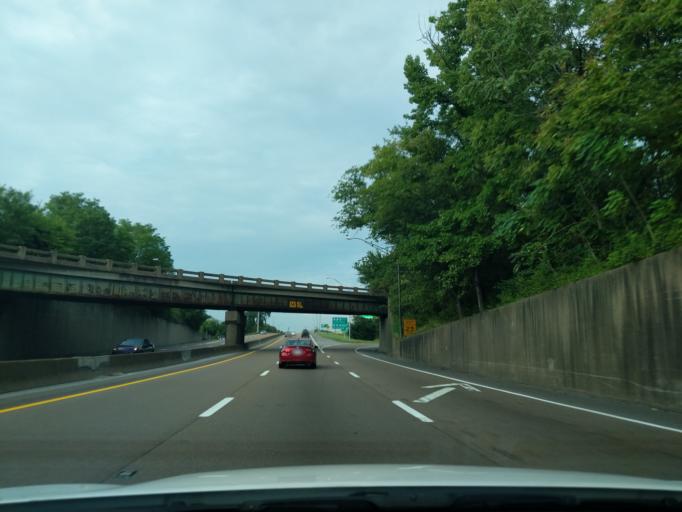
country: US
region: Tennessee
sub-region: Shelby County
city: New South Memphis
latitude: 35.1128
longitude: -90.0742
